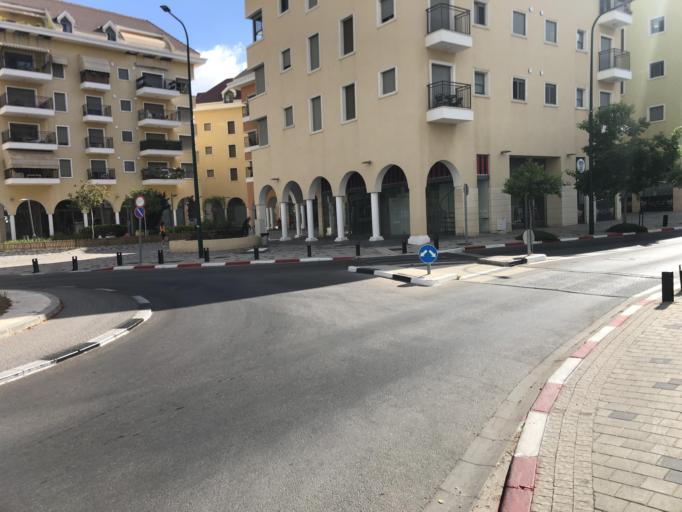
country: IL
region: Central District
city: Yehud
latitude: 32.0295
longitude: 34.8873
